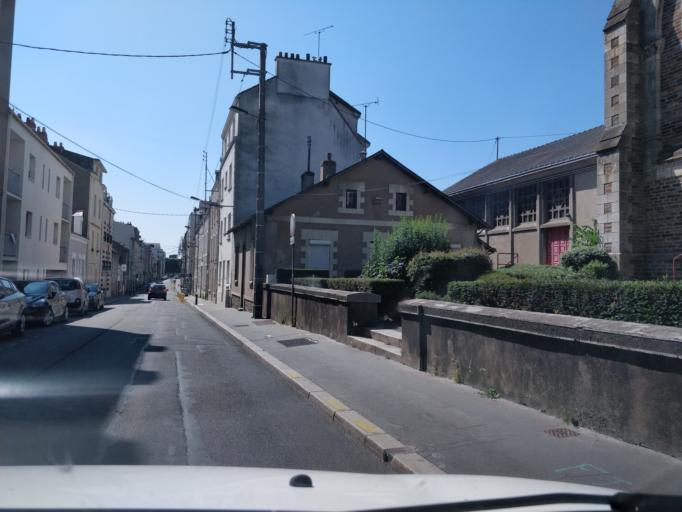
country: FR
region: Pays de la Loire
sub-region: Departement de la Loire-Atlantique
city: Nantes
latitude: 47.2223
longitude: -1.5369
